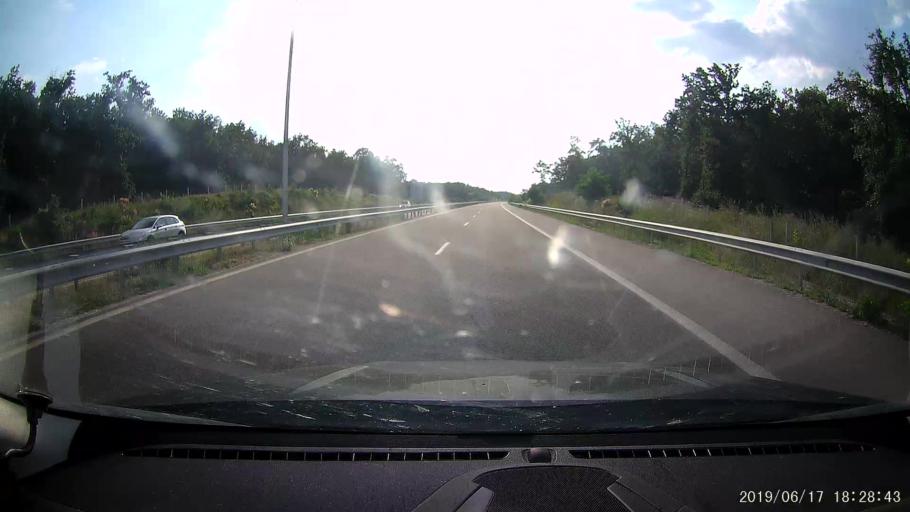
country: BG
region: Khaskovo
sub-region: Obshtina Dimitrovgrad
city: Dimitrovgrad
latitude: 42.0242
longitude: 25.5724
